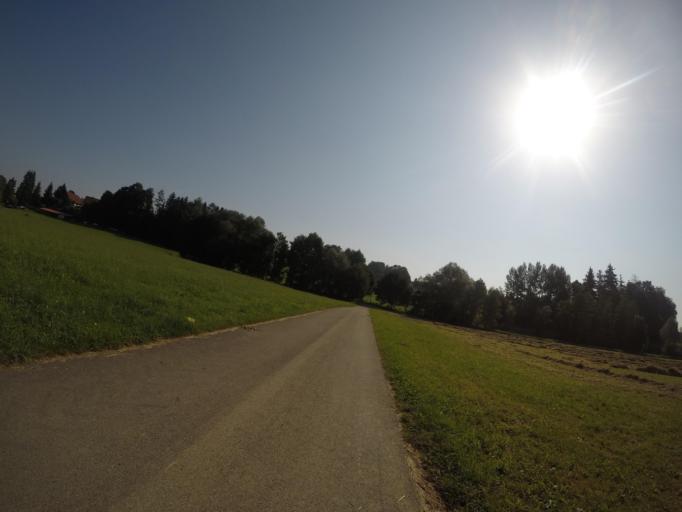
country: DE
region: Baden-Wuerttemberg
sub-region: Tuebingen Region
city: Wain
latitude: 48.2094
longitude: 10.0157
